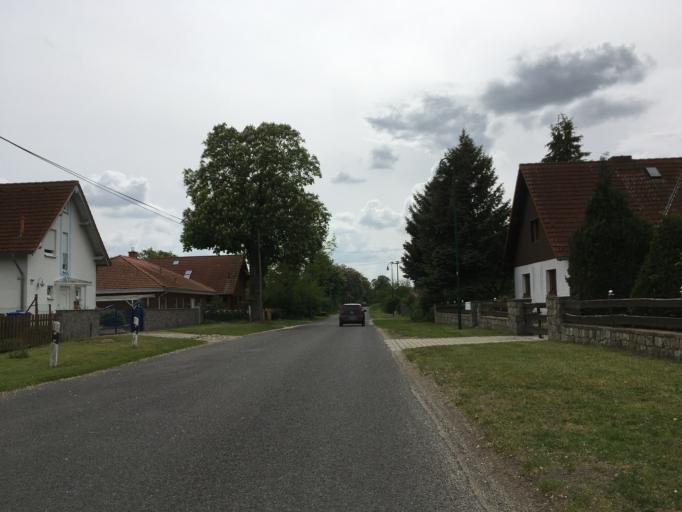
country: DE
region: Brandenburg
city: Melchow
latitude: 52.7180
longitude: 13.7349
